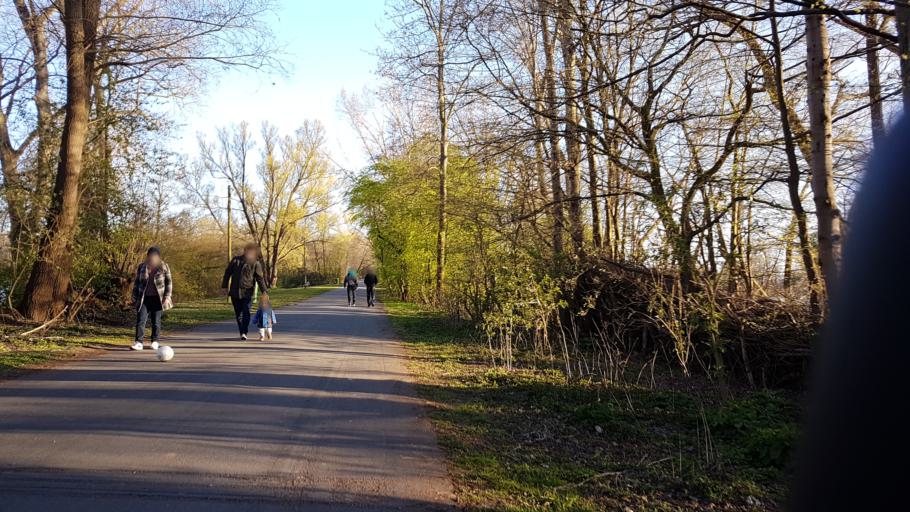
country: DE
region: Lower Saxony
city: Hannover
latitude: 52.3424
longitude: 9.7401
